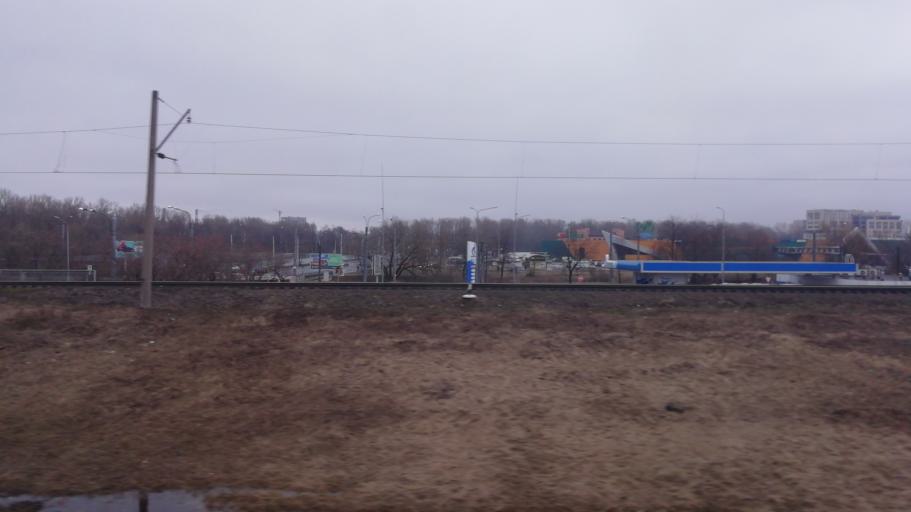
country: RU
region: St.-Petersburg
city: Kupchino
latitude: 59.8780
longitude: 30.3511
